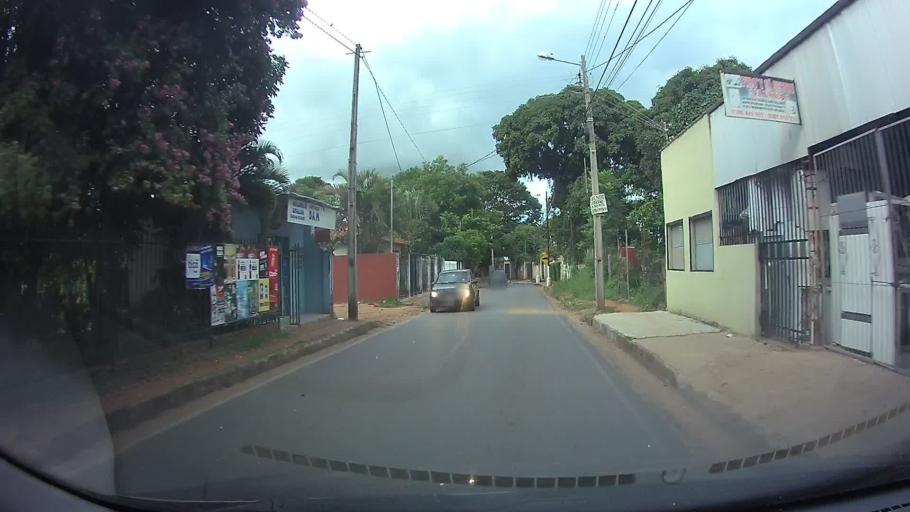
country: PY
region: Central
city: Fernando de la Mora
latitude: -25.3010
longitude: -57.5202
